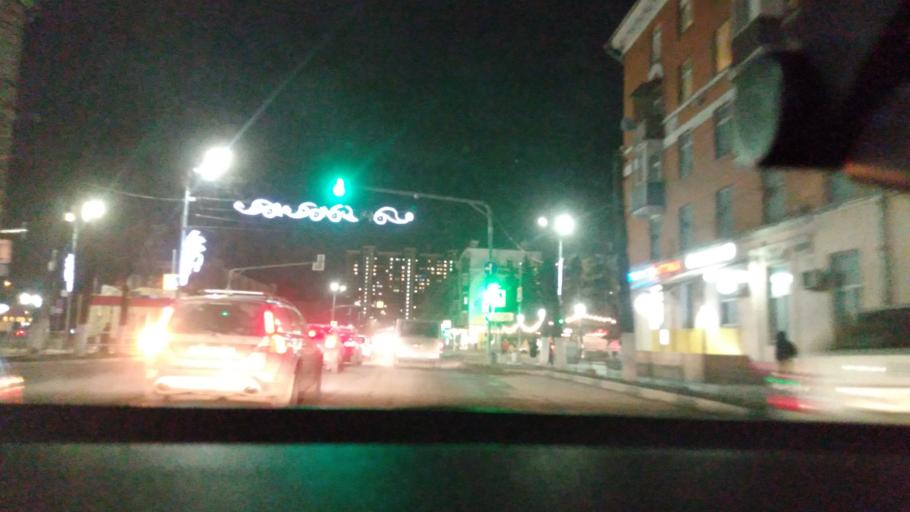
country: RU
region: Moskovskaya
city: Balashikha
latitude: 55.7977
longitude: 37.9344
